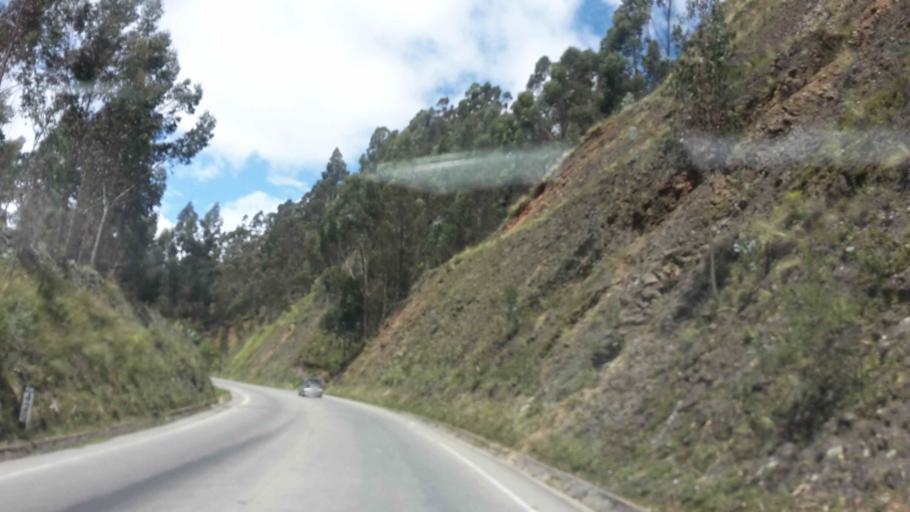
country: BO
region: Cochabamba
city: Colomi
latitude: -17.3181
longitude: -65.8669
